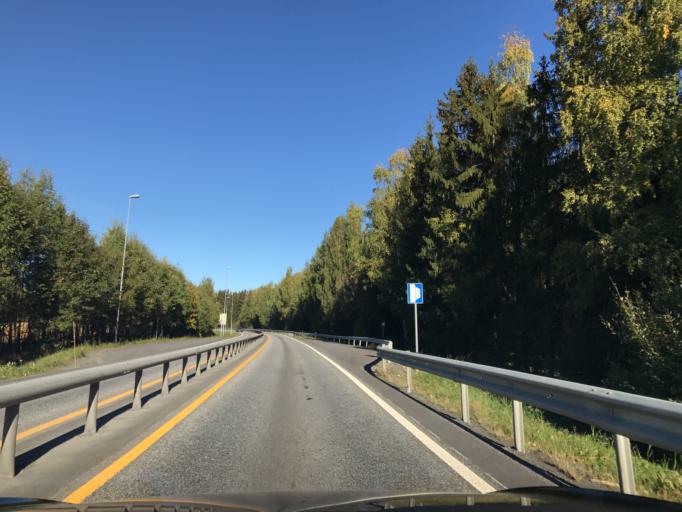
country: NO
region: Hedmark
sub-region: Ringsaker
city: Moelv
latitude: 60.9604
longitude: 10.6221
